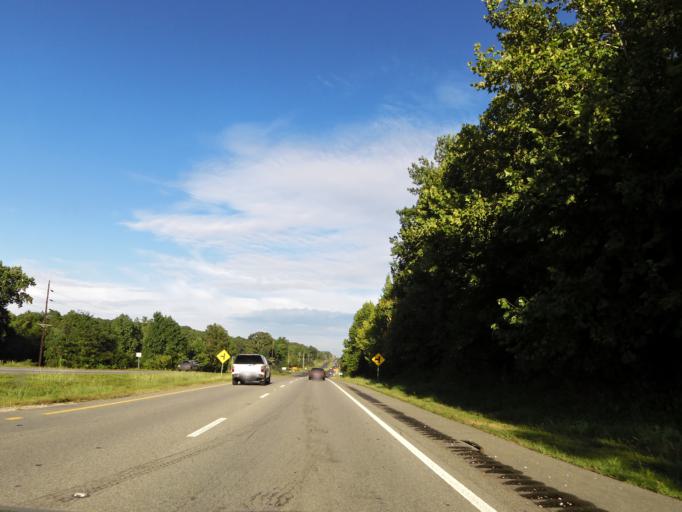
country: US
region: Alabama
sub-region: Lauderdale County
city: Killen
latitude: 34.8597
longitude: -87.5232
